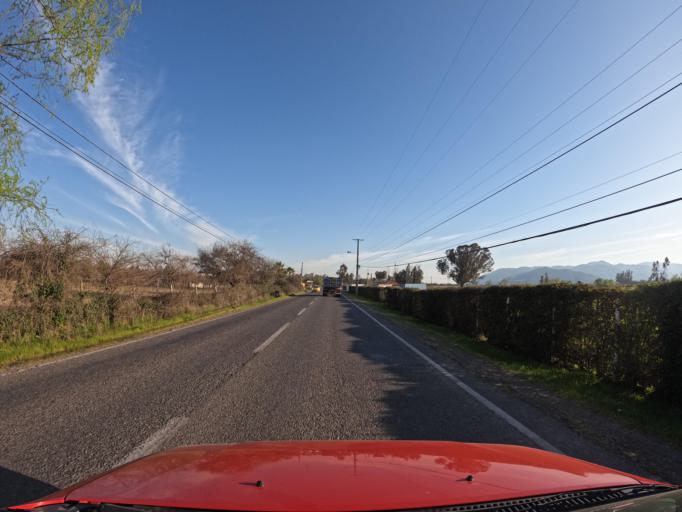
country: CL
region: Maule
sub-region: Provincia de Curico
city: Rauco
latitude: -34.8762
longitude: -71.2679
